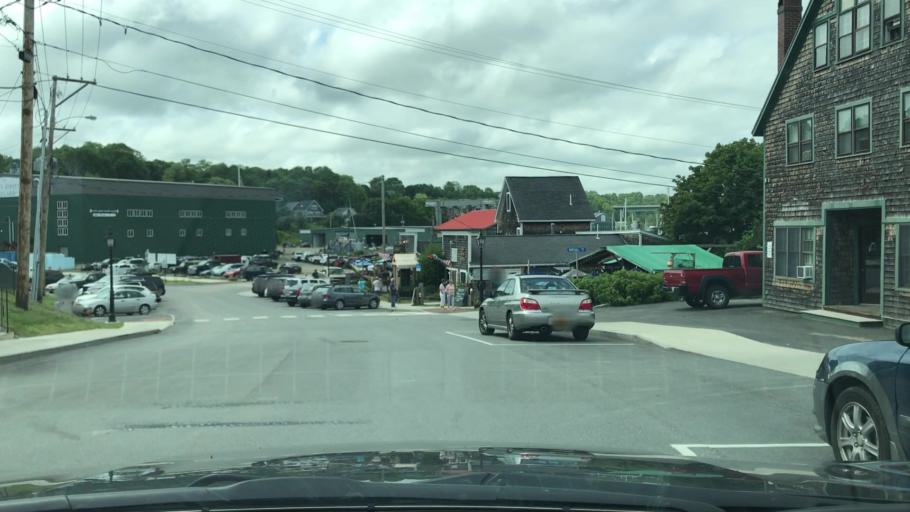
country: US
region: Maine
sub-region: Waldo County
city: Belfast
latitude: 44.4282
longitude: -69.0050
